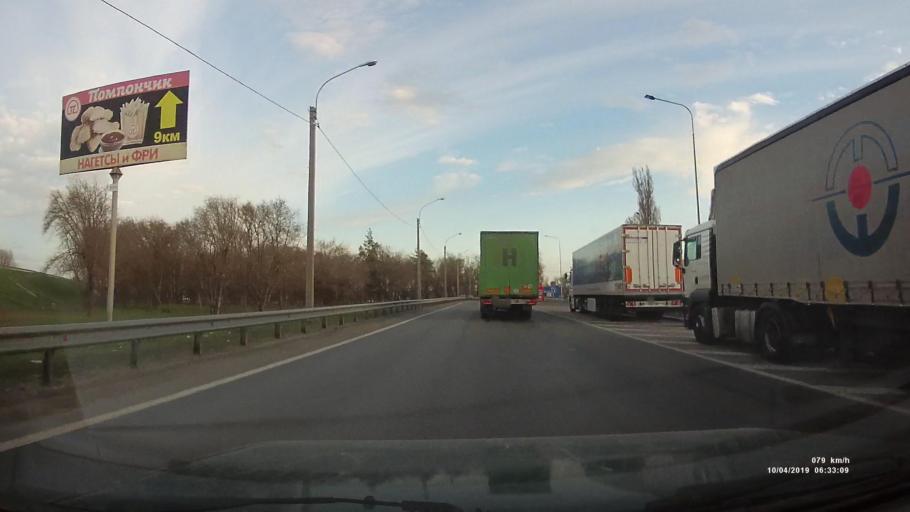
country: RU
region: Rostov
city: Aksay
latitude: 47.2834
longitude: 39.8496
